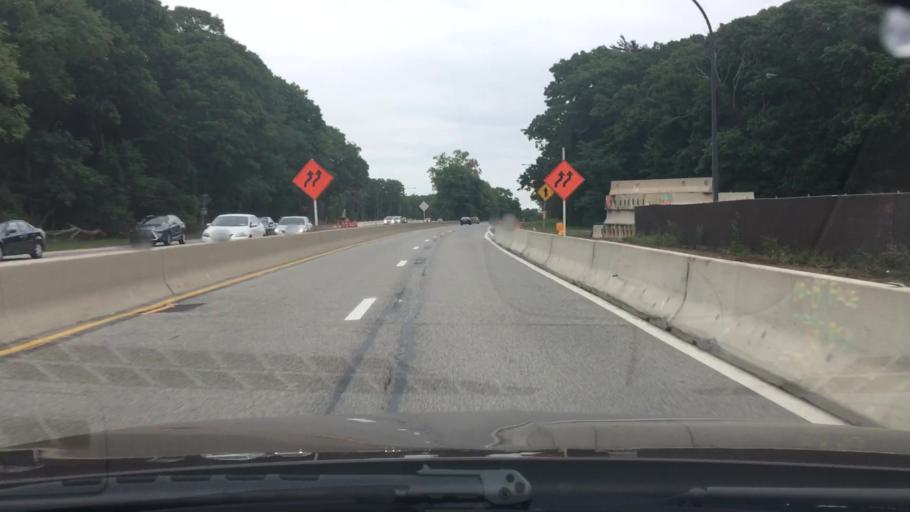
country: US
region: New York
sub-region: Suffolk County
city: Dix Hills
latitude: 40.8252
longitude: -73.3389
